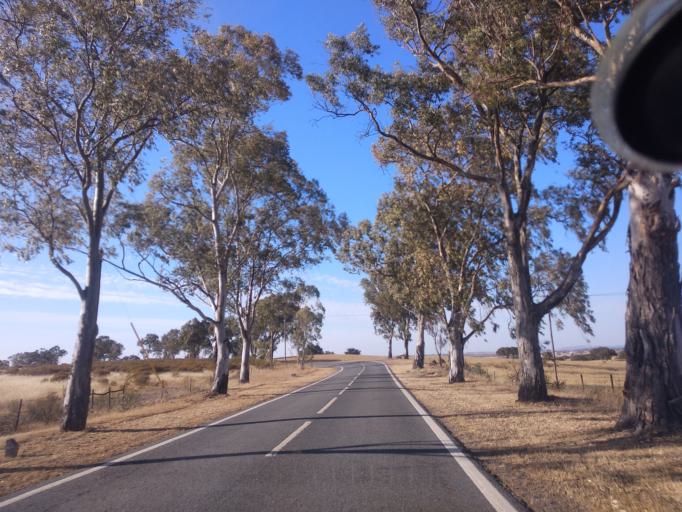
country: PT
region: Beja
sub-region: Almodovar
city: Almodovar
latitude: 37.4506
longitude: -7.9964
